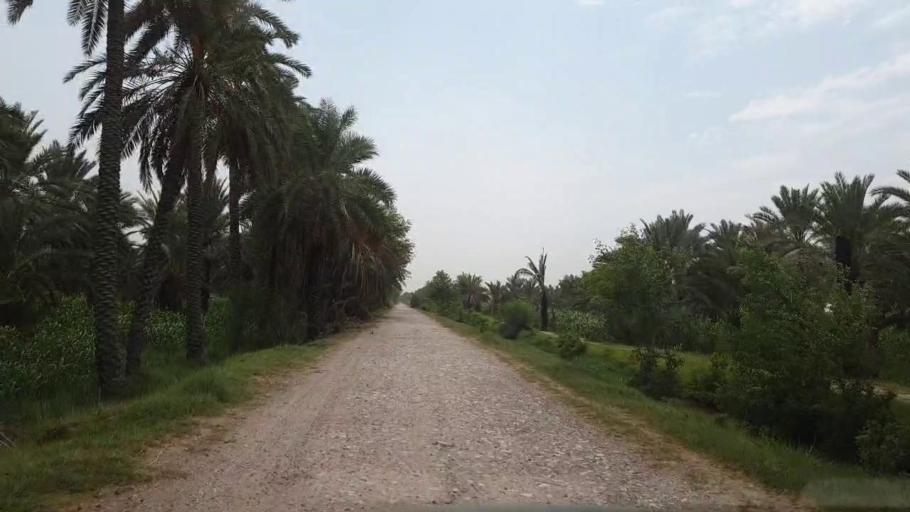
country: PK
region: Sindh
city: Pir jo Goth
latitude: 27.4956
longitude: 68.6000
